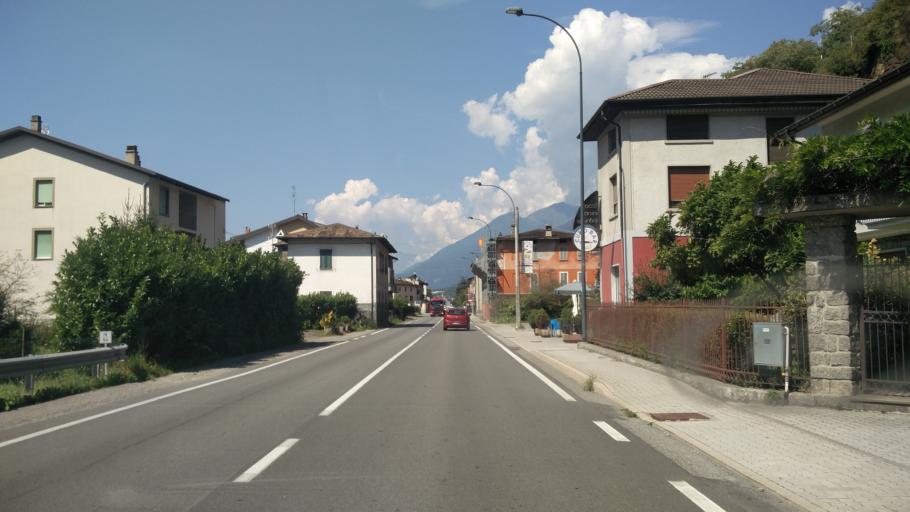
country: IT
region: Lombardy
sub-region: Provincia di Sondrio
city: San Giacomo
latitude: 46.1597
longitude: 10.0302
